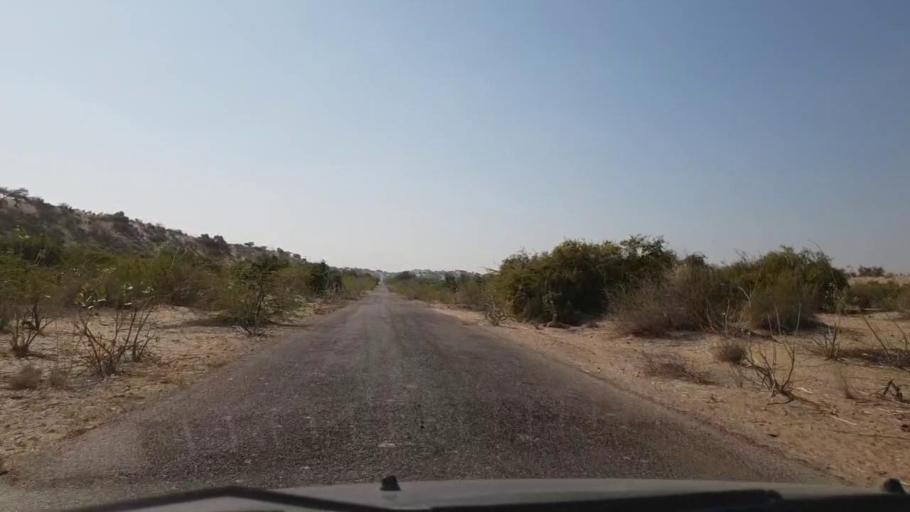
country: PK
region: Sindh
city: Diplo
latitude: 24.5328
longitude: 69.6345
